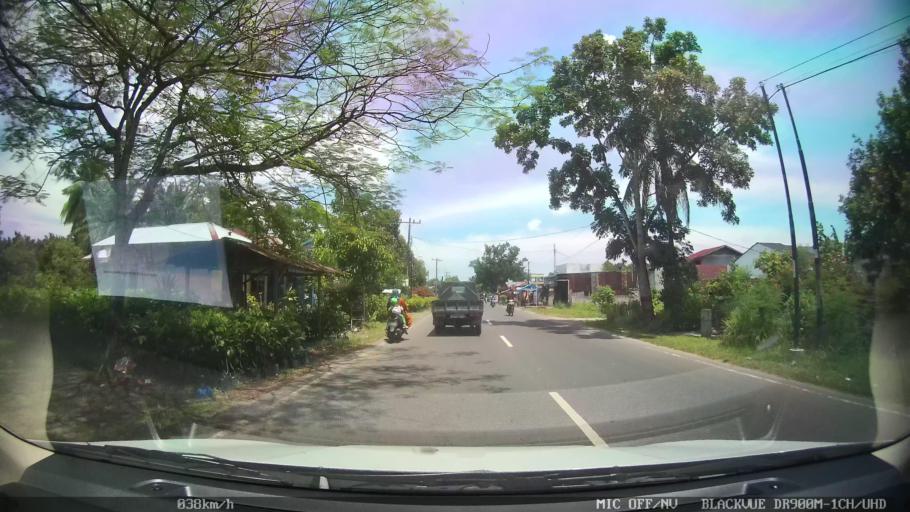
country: ID
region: North Sumatra
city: Binjai
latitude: 3.5955
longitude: 98.5012
